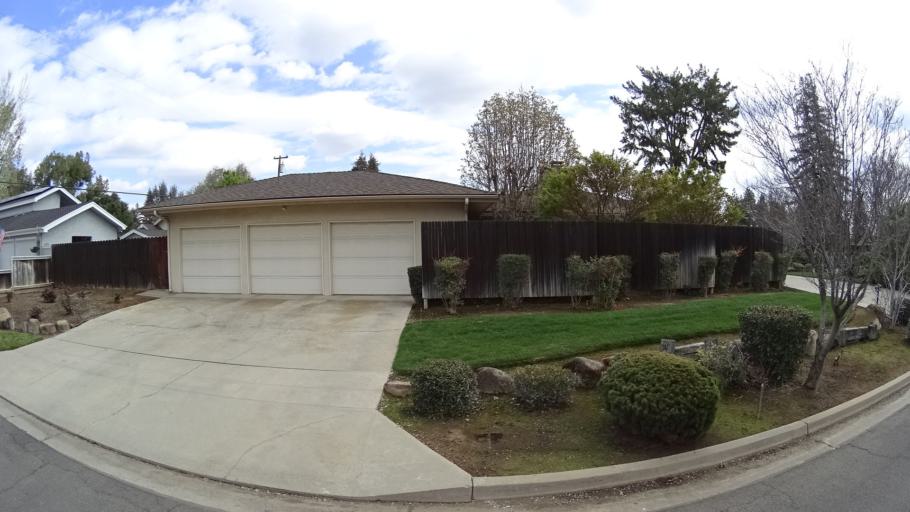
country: US
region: California
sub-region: Fresno County
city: Fresno
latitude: 36.8261
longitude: -119.8422
